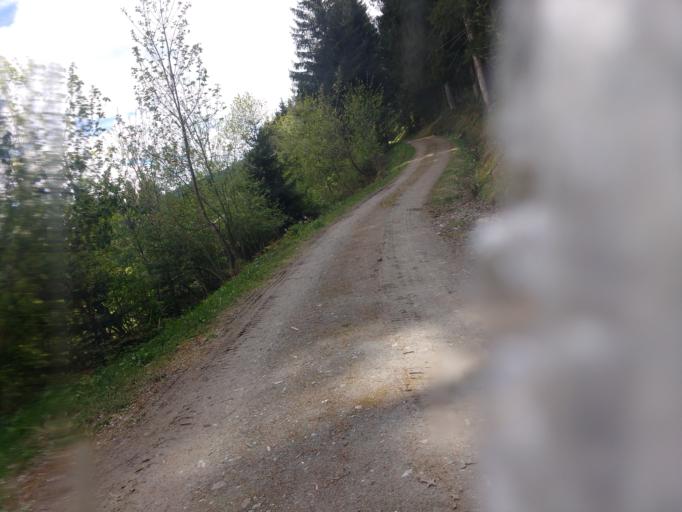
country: AT
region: Tyrol
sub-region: Politischer Bezirk Innsbruck Land
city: Rinn
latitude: 47.2439
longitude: 11.4938
